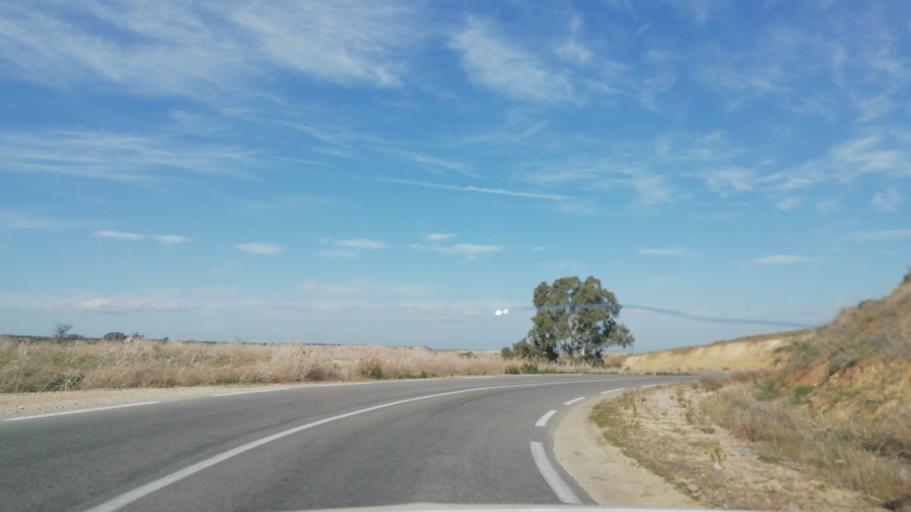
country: DZ
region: Tlemcen
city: Chetouane
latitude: 34.9621
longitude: -1.2472
